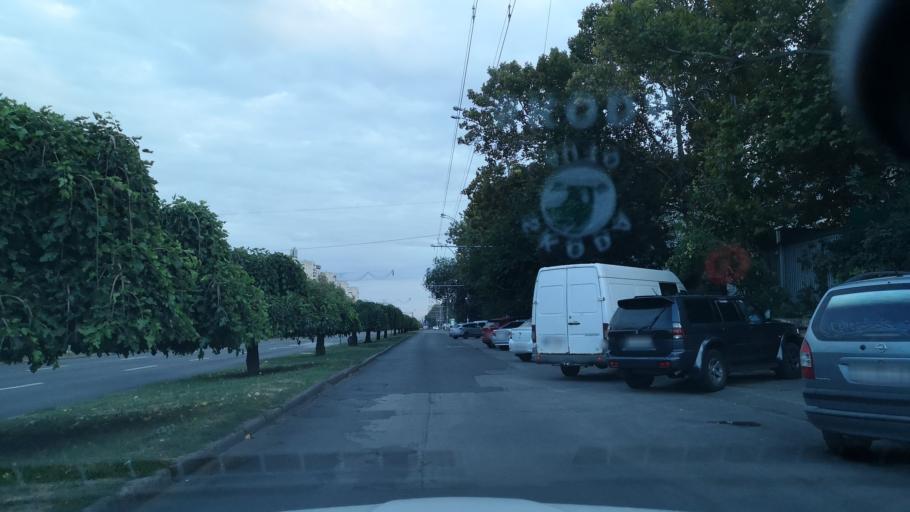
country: MD
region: Chisinau
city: Chisinau
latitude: 46.9899
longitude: 28.8518
